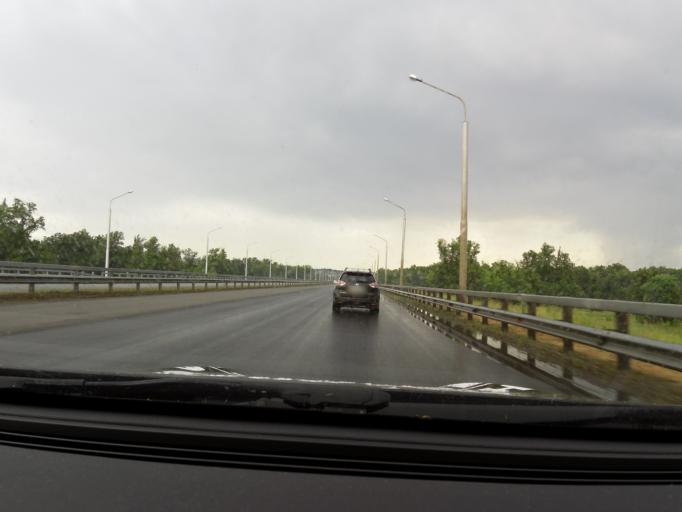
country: RU
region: Bashkortostan
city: Mikhaylovka
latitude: 54.7858
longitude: 55.9095
